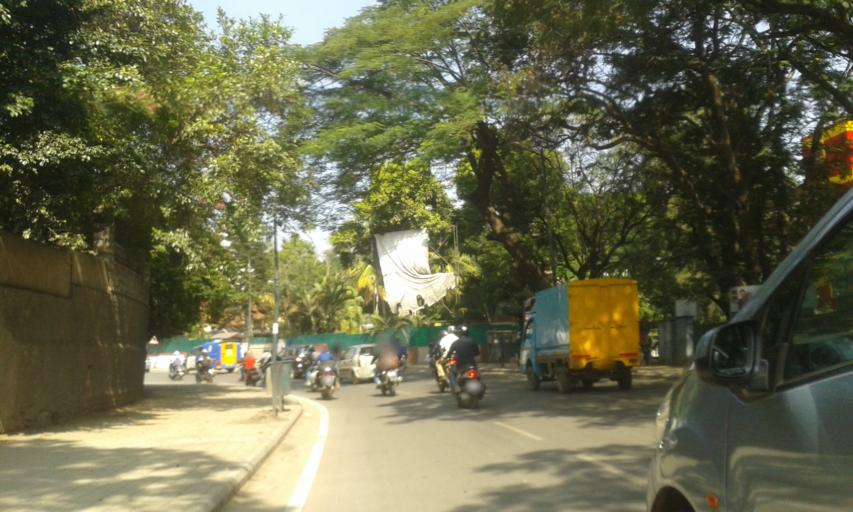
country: IN
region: Karnataka
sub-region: Bangalore Urban
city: Bangalore
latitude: 12.9720
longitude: 77.6043
